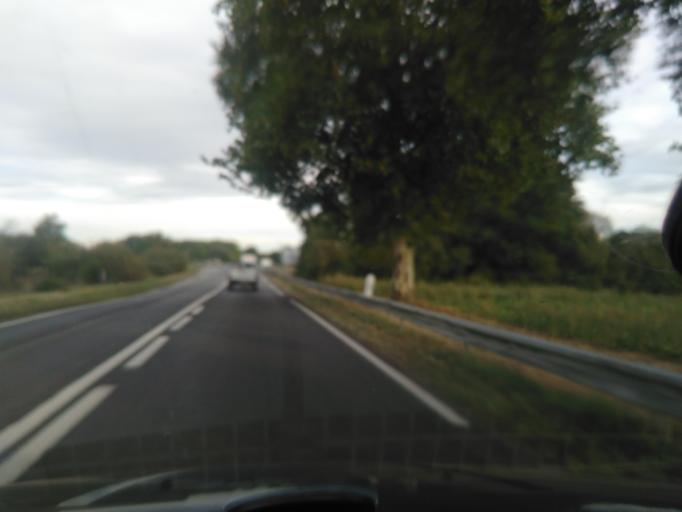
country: FR
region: Picardie
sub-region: Departement de l'Aisne
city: Laon
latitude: 49.5490
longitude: 3.5977
